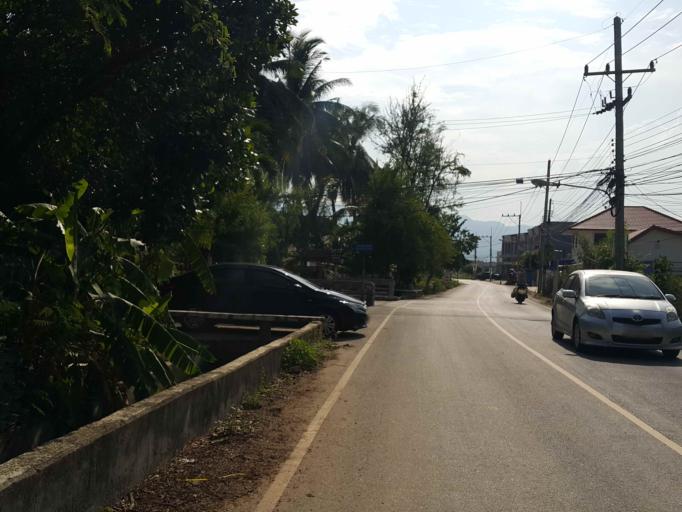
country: TH
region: Chiang Mai
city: San Sai
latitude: 18.8303
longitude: 99.0308
